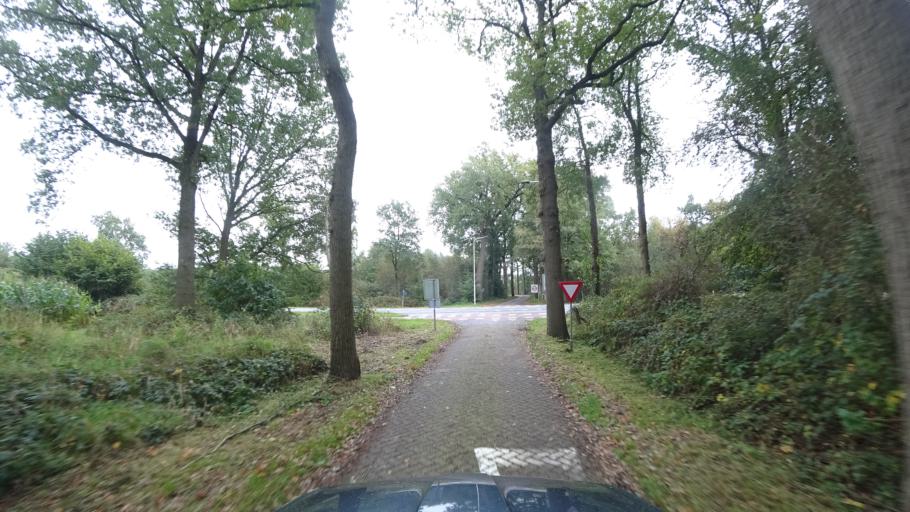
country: NL
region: Gelderland
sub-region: Gemeente Nijkerk
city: Nijkerk
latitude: 52.2439
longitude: 5.5262
